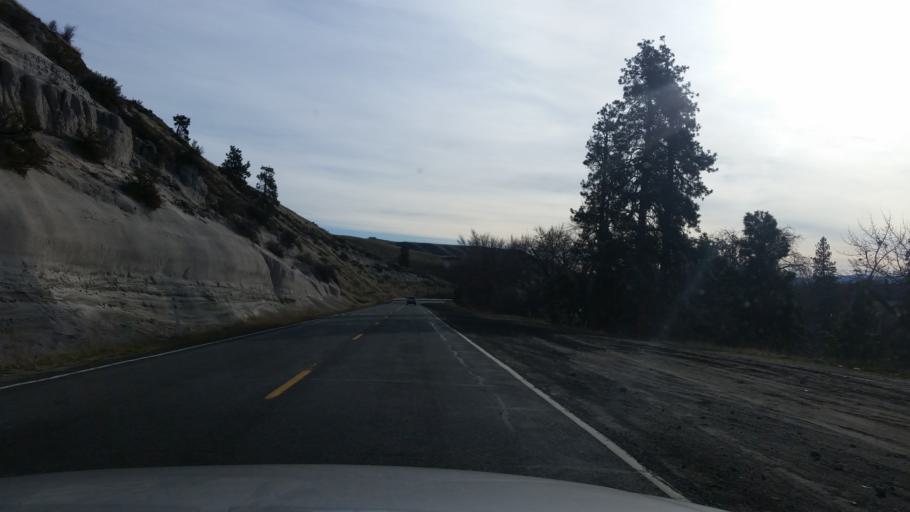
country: US
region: Washington
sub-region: Kittitas County
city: Ellensburg
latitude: 47.1009
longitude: -120.6953
